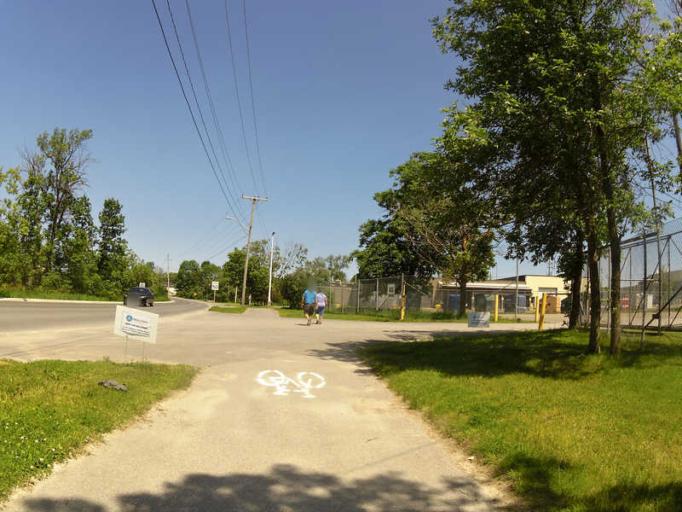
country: CA
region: Ontario
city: Peterborough
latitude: 44.4190
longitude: -78.2675
